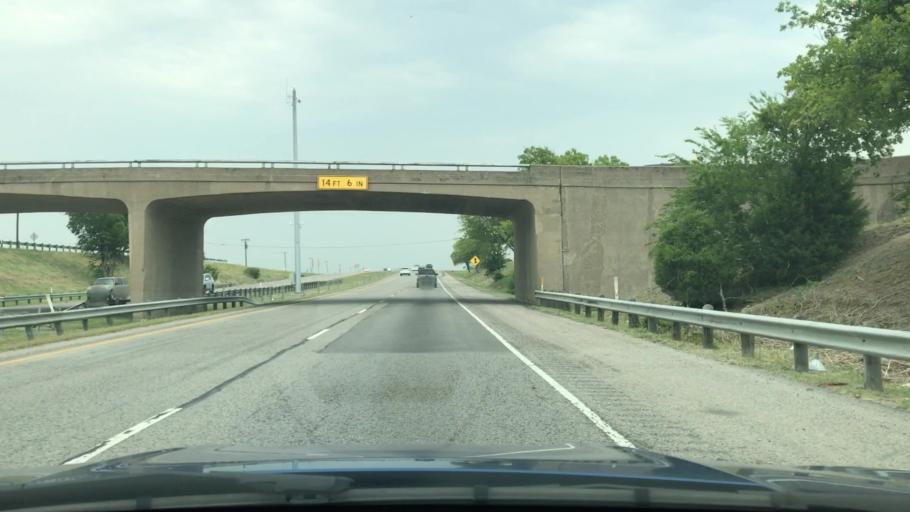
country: US
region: Texas
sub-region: Kaufman County
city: Forney
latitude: 32.7409
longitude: -96.4303
